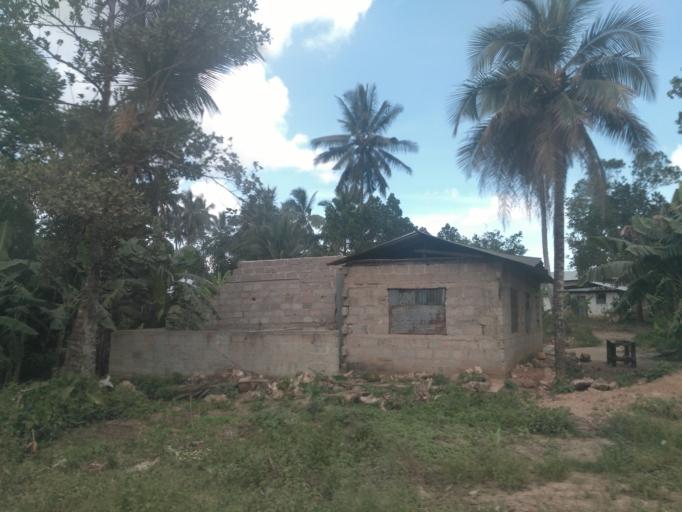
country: TZ
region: Zanzibar North
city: Gamba
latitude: -5.9777
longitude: 39.2941
